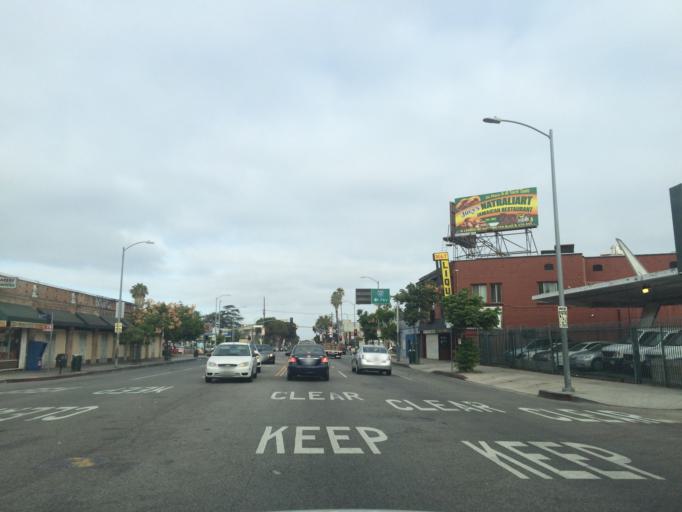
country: US
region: California
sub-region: Los Angeles County
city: View Park-Windsor Hills
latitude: 34.0399
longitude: -118.3295
